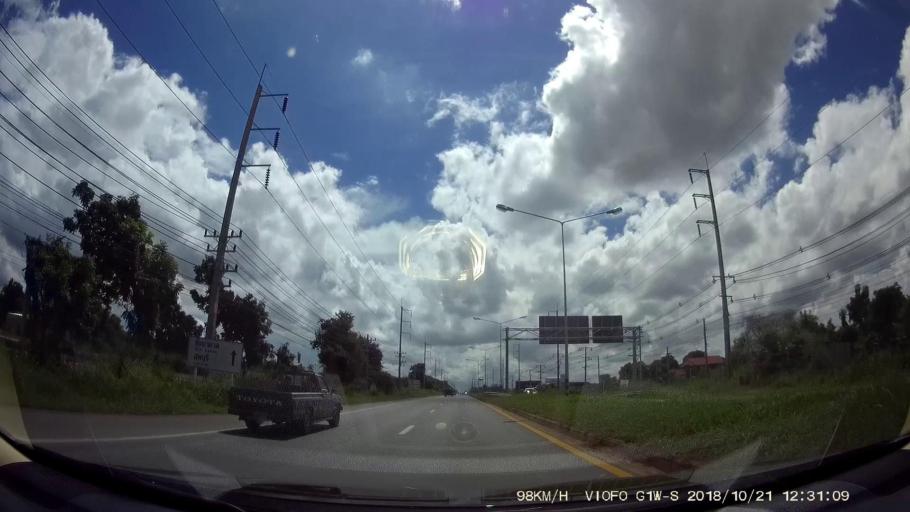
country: TH
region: Nakhon Ratchasima
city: Dan Khun Thot
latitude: 15.1609
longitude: 101.7362
